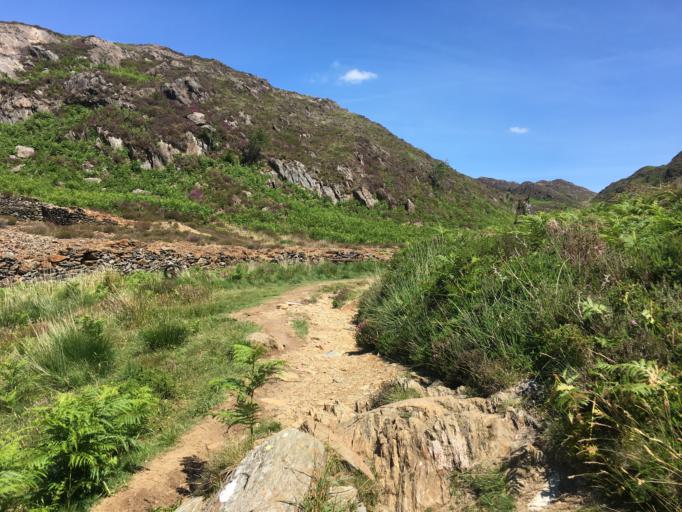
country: GB
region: Wales
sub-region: Gwynedd
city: Penrhyndeudraeth
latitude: 53.0049
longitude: -4.0834
